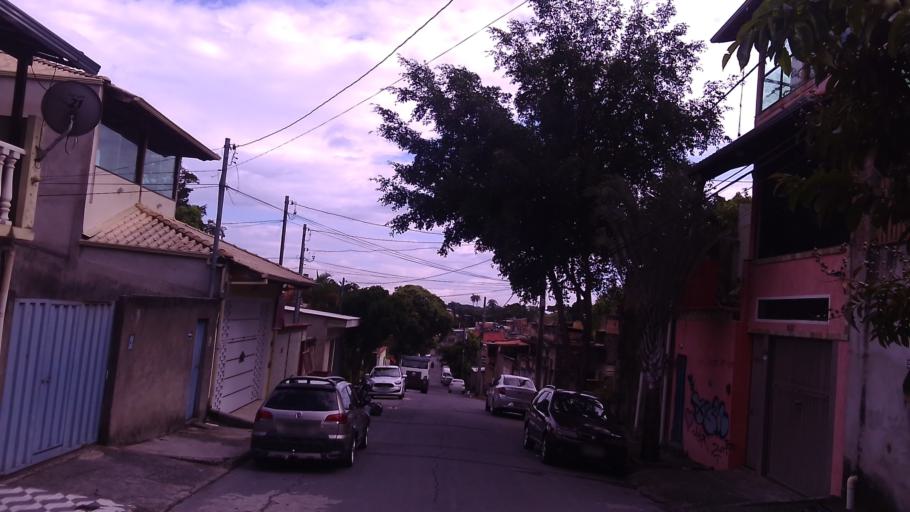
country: BR
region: Minas Gerais
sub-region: Contagem
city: Contagem
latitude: -19.9147
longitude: -44.0203
